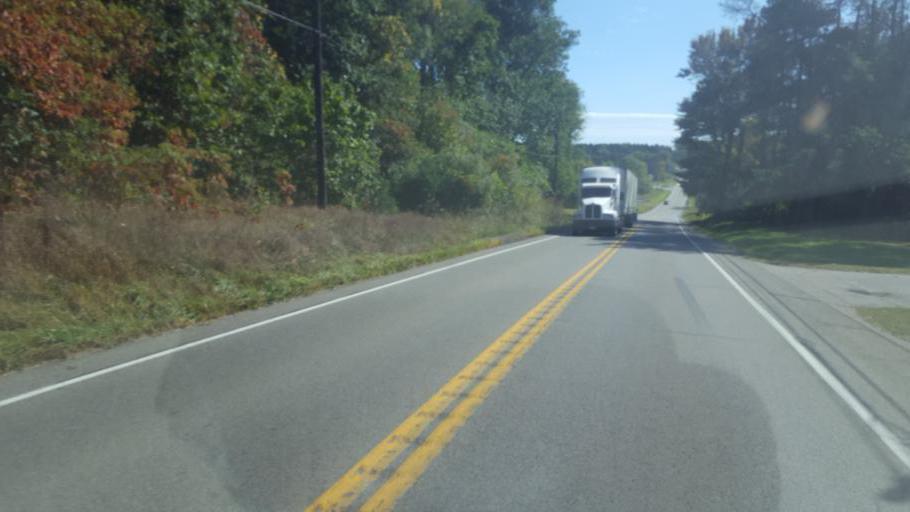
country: US
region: Pennsylvania
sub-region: Mercer County
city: Reynolds Heights
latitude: 41.3638
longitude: -80.3553
